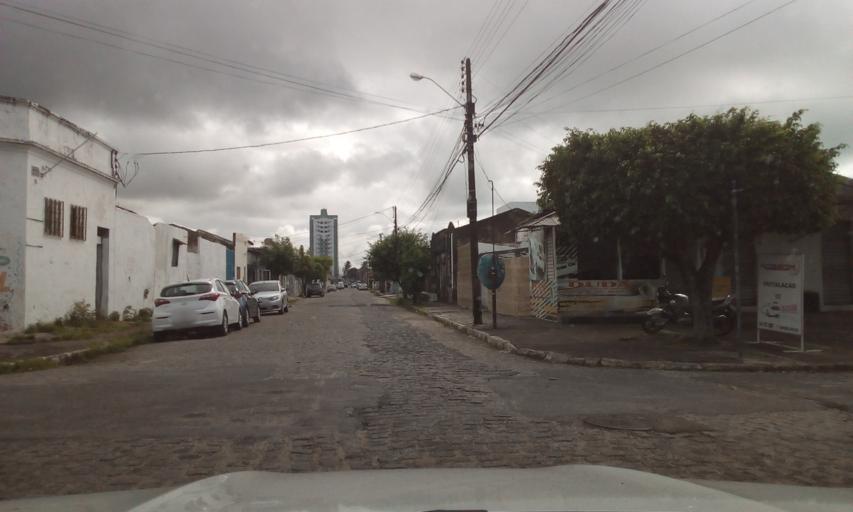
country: BR
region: Paraiba
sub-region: Joao Pessoa
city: Joao Pessoa
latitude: -7.1316
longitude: -34.8752
